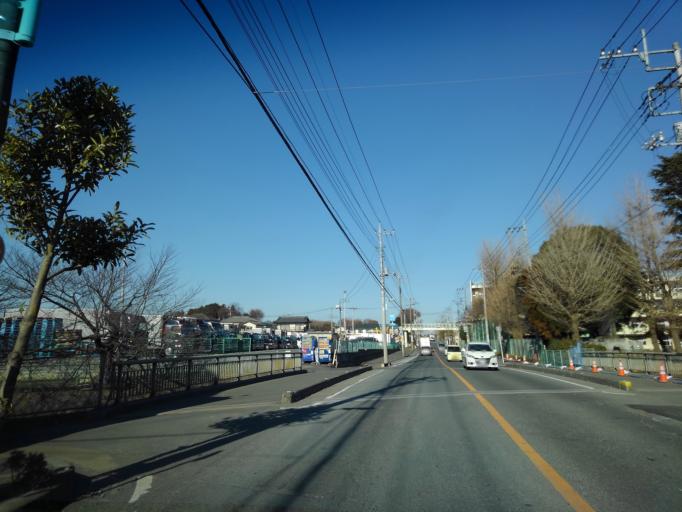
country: JP
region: Saitama
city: Oi
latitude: 35.8049
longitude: 139.5219
